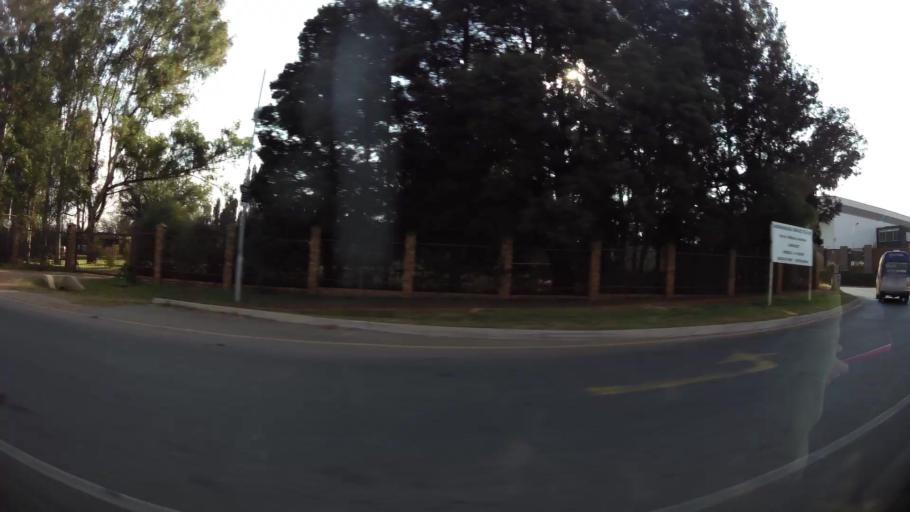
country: ZA
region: Gauteng
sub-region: Ekurhuleni Metropolitan Municipality
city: Tembisa
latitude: -26.0818
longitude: 28.2825
